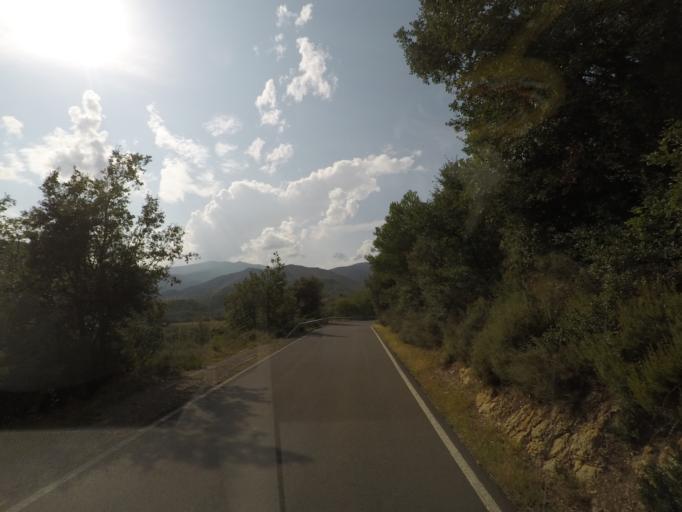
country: ES
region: Aragon
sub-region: Provincia de Huesca
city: Laspuna
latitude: 42.5041
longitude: 0.1336
